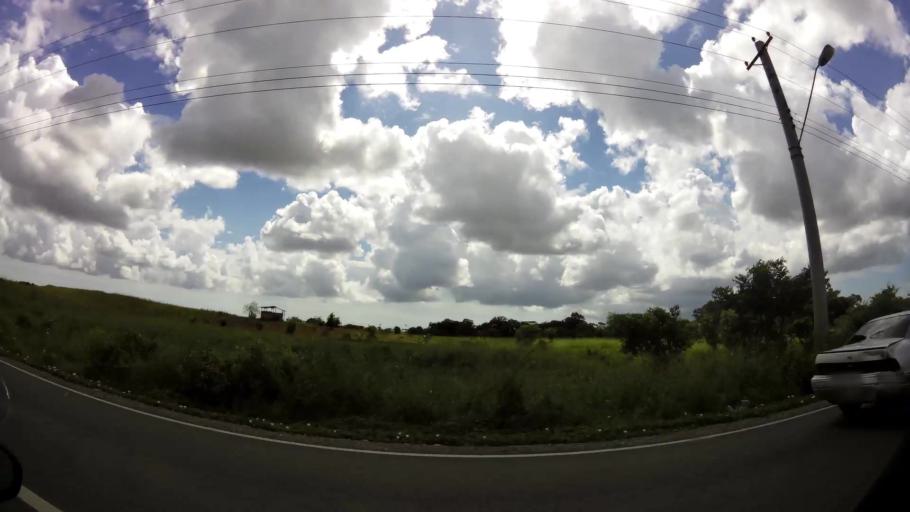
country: TT
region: Penal/Debe
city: Debe
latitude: 10.2226
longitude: -61.4790
